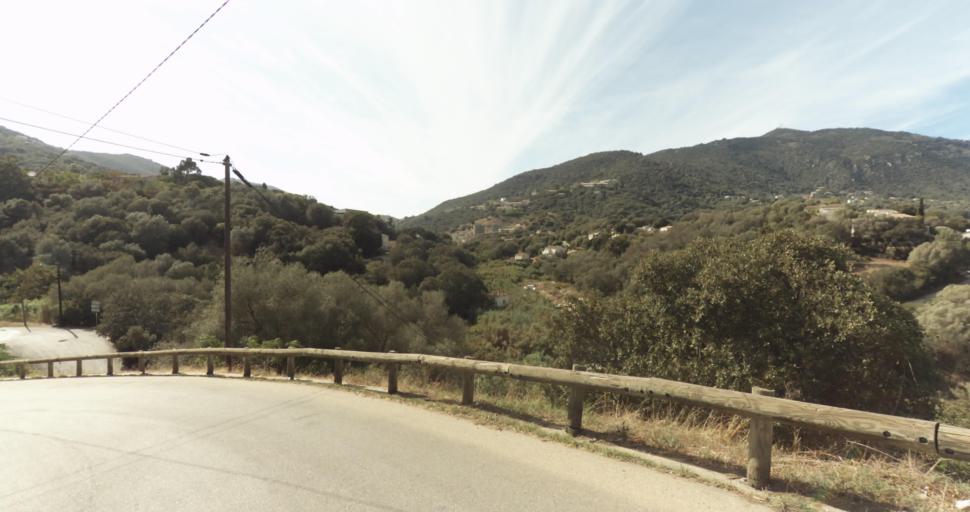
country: FR
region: Corsica
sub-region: Departement de la Corse-du-Sud
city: Ajaccio
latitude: 41.9316
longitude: 8.7290
